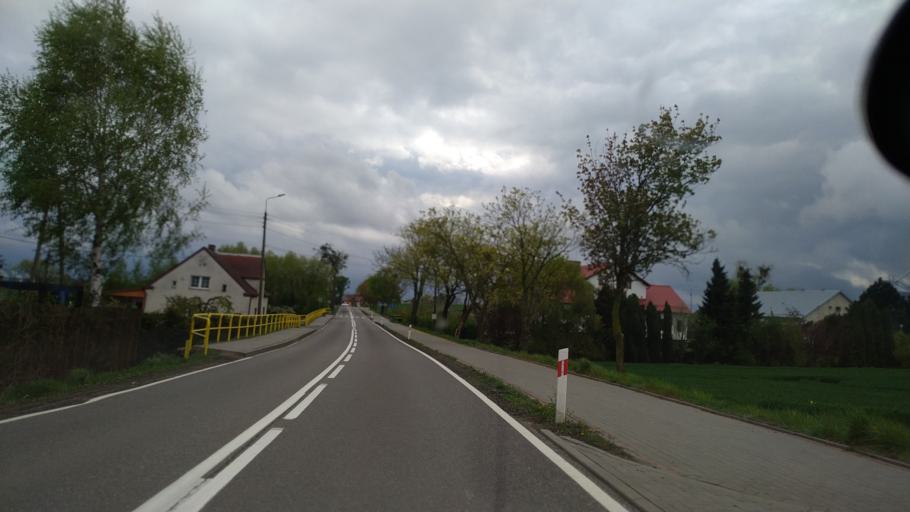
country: PL
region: Pomeranian Voivodeship
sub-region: Powiat kwidzynski
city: Kwidzyn
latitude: 53.7742
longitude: 18.9524
